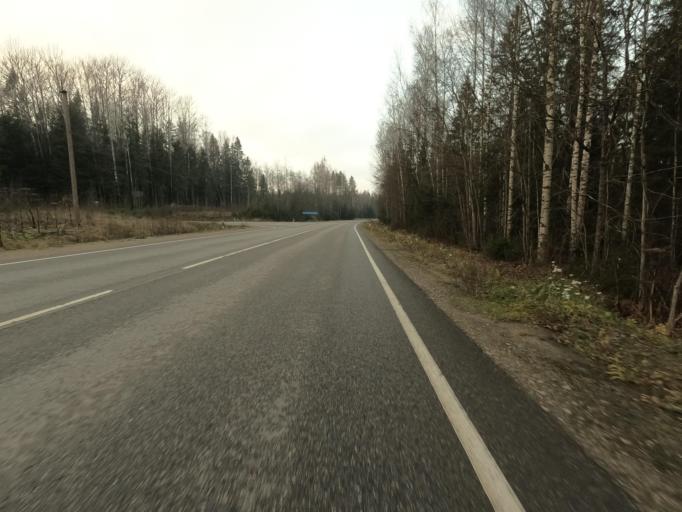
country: RU
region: Leningrad
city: Kirovsk
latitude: 59.8209
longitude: 30.9786
